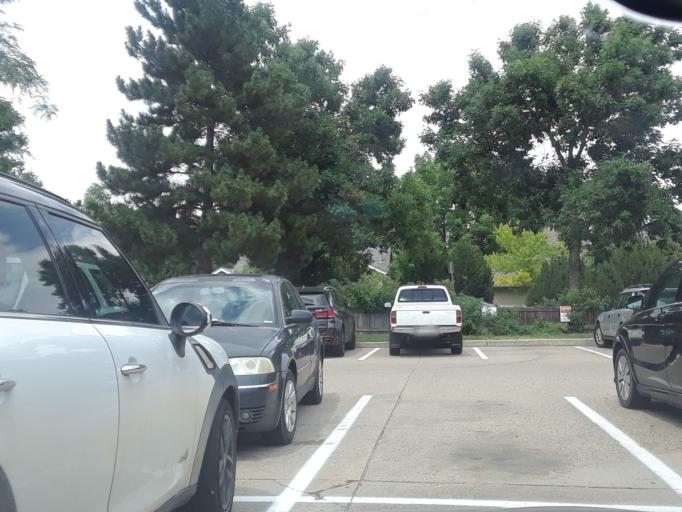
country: US
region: Colorado
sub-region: Boulder County
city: Boulder
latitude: 40.0478
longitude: -105.2812
